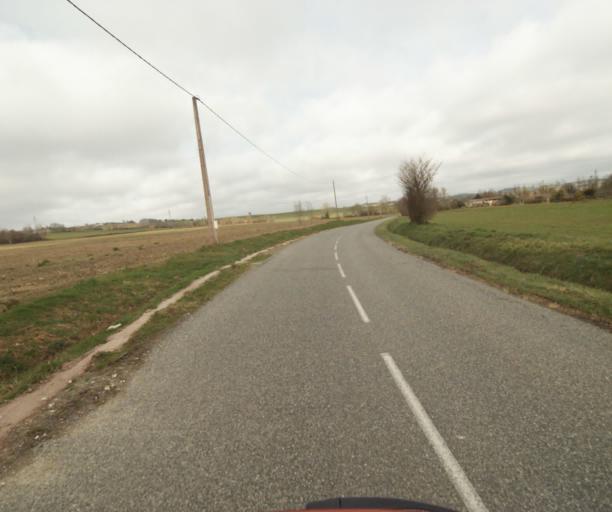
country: FR
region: Midi-Pyrenees
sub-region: Departement de l'Ariege
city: Pamiers
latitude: 43.1128
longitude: 1.5458
